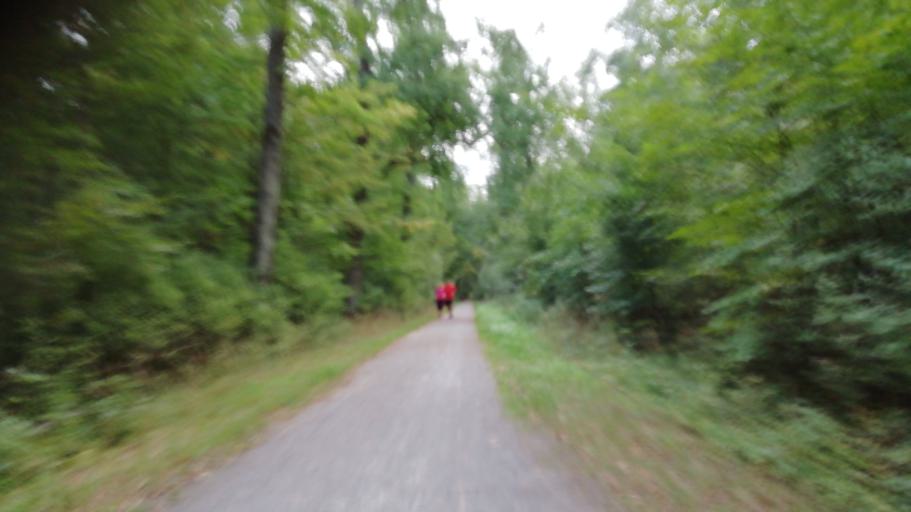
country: DE
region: Baden-Wuerttemberg
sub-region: Regierungsbezirk Stuttgart
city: Stuttgart Feuerbach
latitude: 48.8250
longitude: 9.1441
